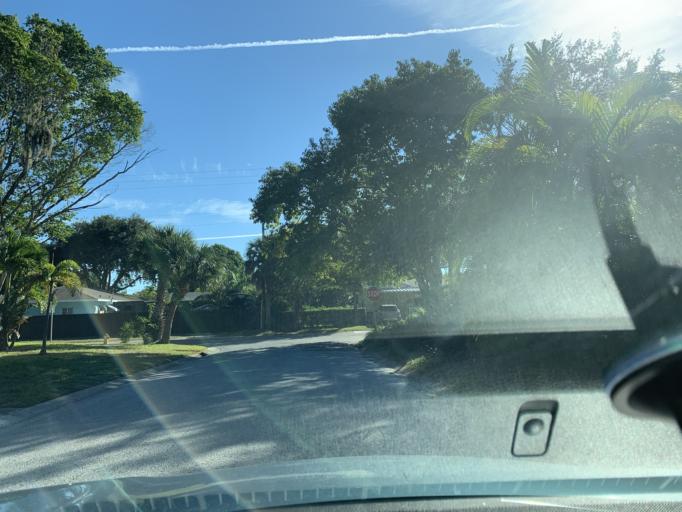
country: US
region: Florida
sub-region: Pinellas County
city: Gulfport
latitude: 27.7451
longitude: -82.6977
